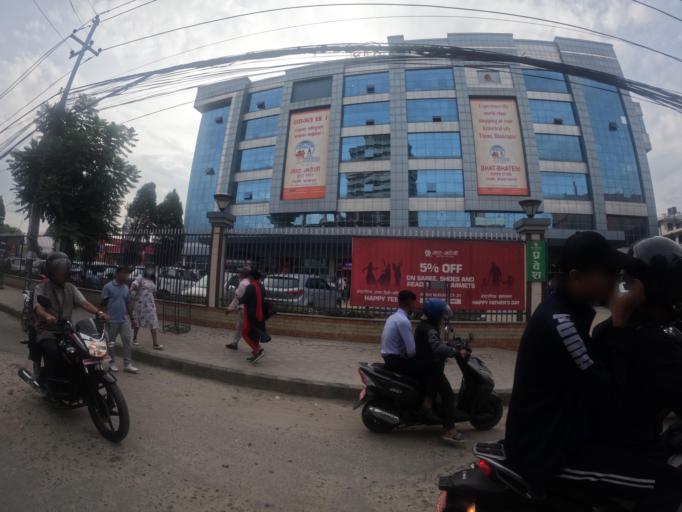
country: NP
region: Central Region
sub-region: Bagmati Zone
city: Bhaktapur
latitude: 27.6753
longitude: 85.3978
